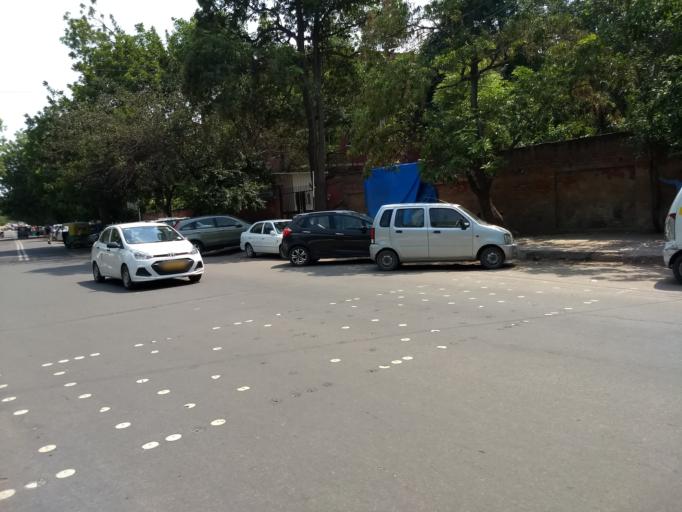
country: IN
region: NCT
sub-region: New Delhi
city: New Delhi
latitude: 28.5473
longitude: 77.2069
